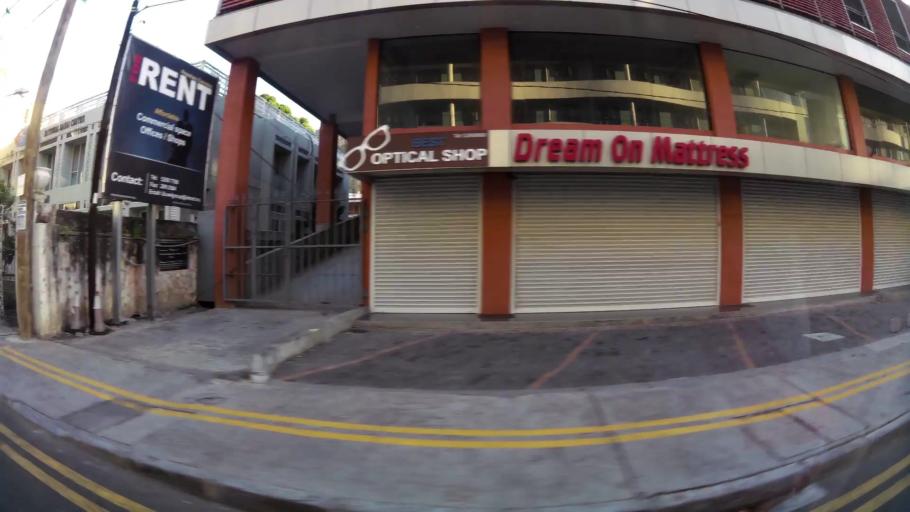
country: MU
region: Port Louis
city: Port Louis
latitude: -20.1696
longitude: 57.5017
